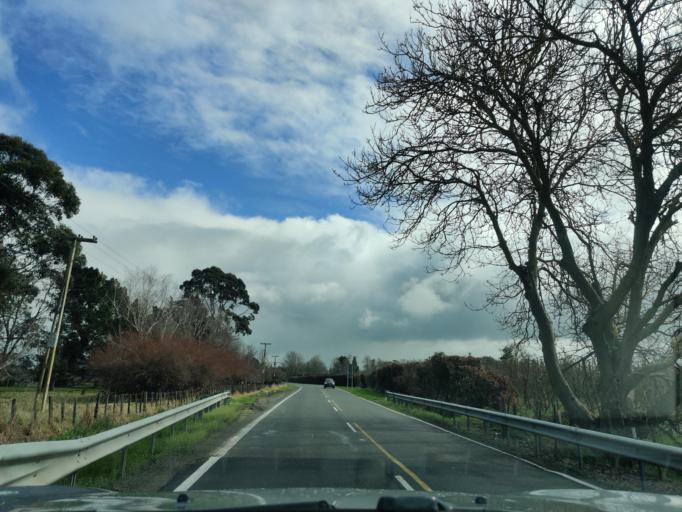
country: NZ
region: Hawke's Bay
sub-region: Hastings District
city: Hastings
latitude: -39.6782
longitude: 176.8596
